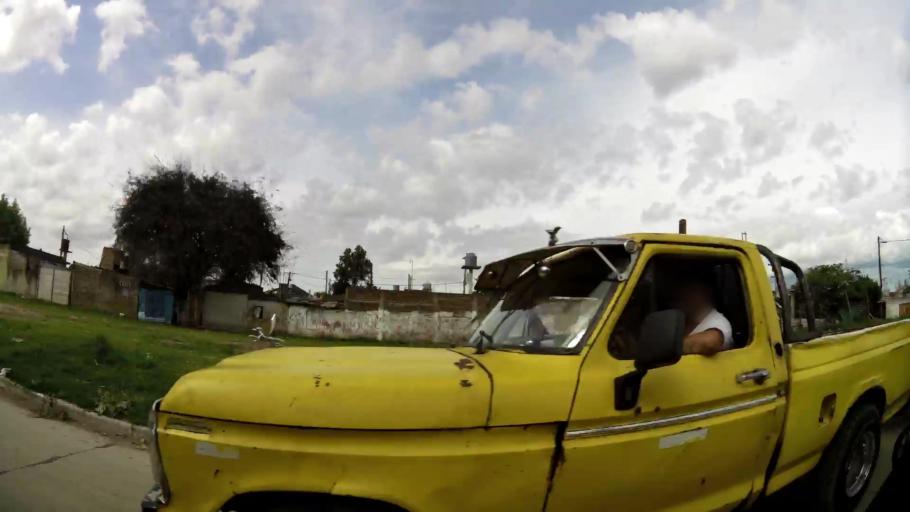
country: AR
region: Buenos Aires
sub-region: Partido de Quilmes
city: Quilmes
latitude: -34.7601
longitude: -58.2478
